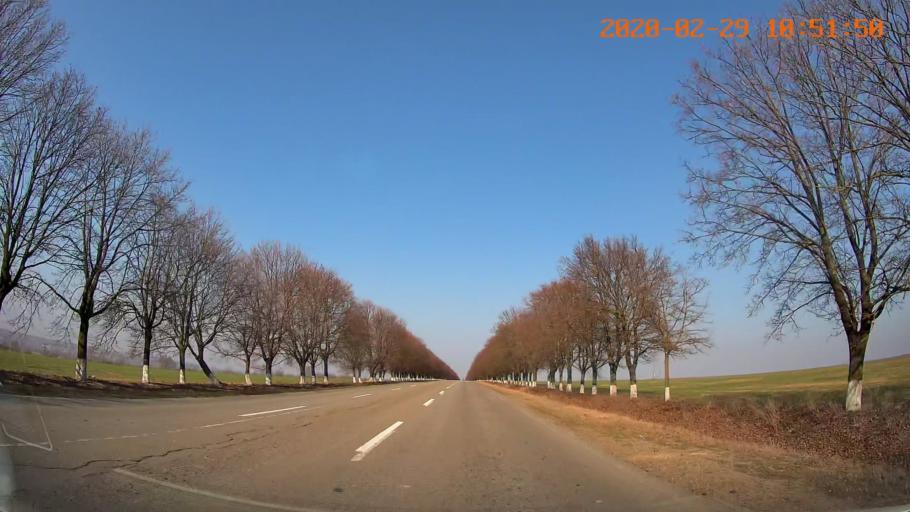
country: MD
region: Telenesti
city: Grigoriopol
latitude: 47.0978
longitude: 29.3587
